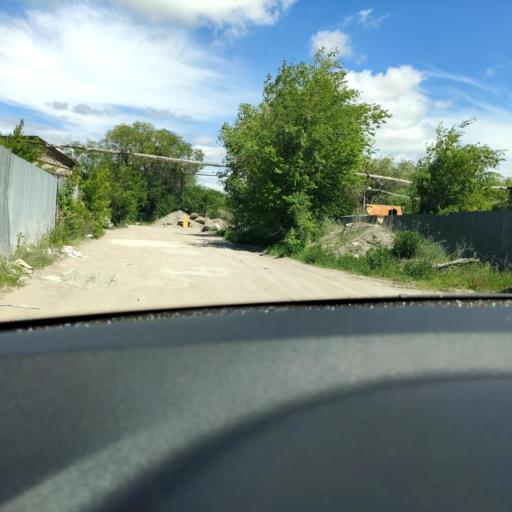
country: RU
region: Samara
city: Samara
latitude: 53.1781
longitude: 50.2113
